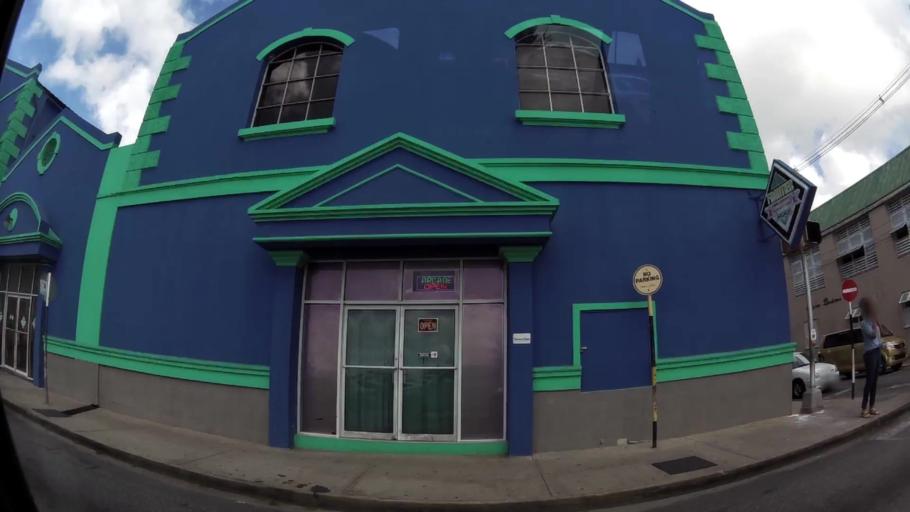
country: BB
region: Saint Michael
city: Bridgetown
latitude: 13.0969
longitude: -59.6186
